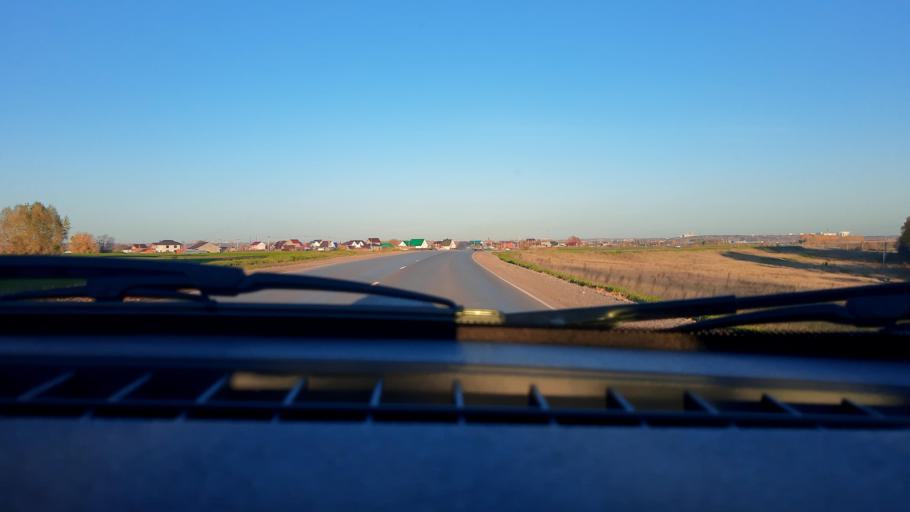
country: RU
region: Bashkortostan
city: Mikhaylovka
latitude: 54.8335
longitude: 55.9349
